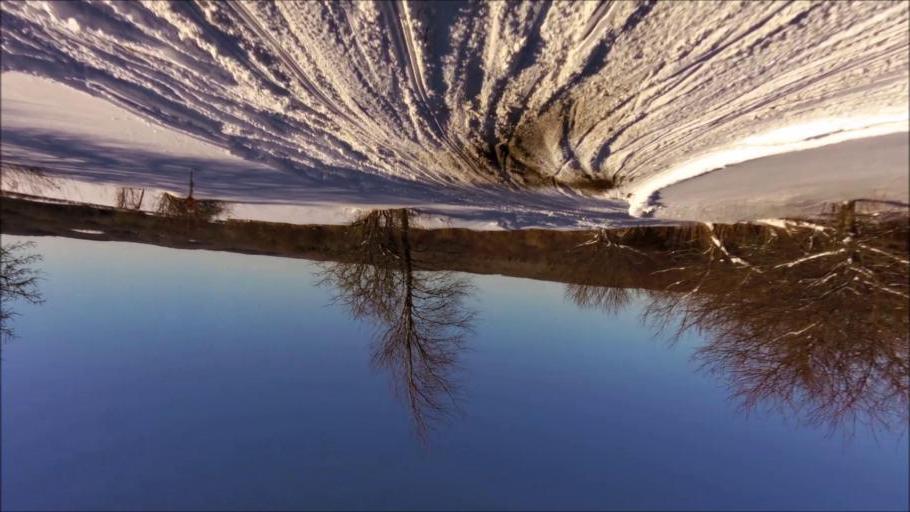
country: US
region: New York
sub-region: Chautauqua County
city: Mayville
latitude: 42.2818
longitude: -79.4246
